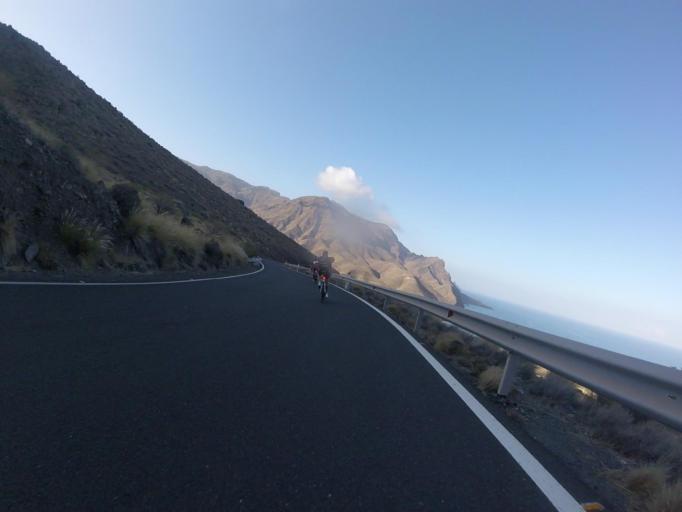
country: ES
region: Canary Islands
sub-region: Provincia de Las Palmas
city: Agaete
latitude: 28.0592
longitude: -15.7300
